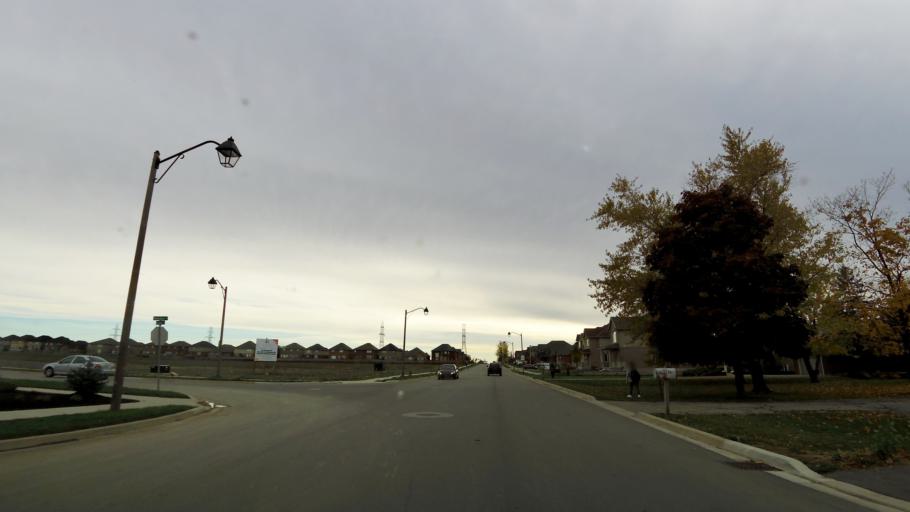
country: CA
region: Ontario
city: Hamilton
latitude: 43.1783
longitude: -79.8066
